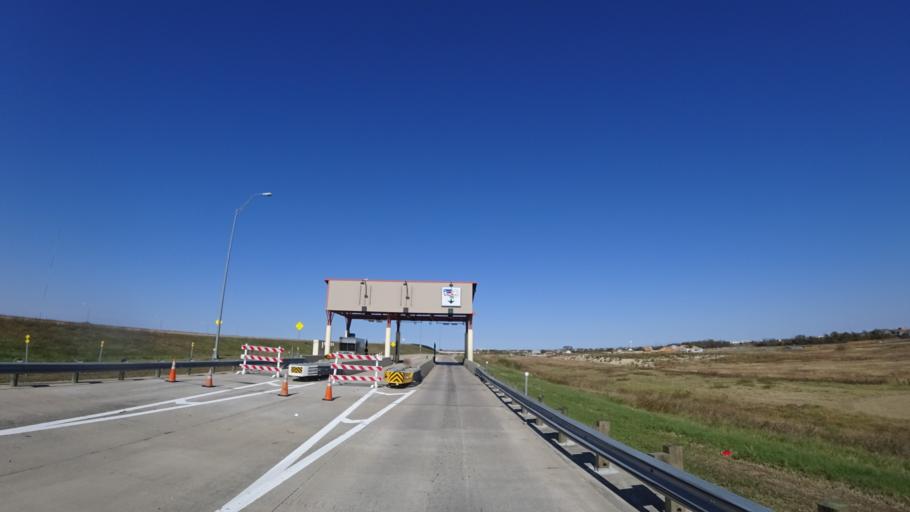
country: US
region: Texas
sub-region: Williamson County
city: Hutto
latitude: 30.5306
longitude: -97.5754
